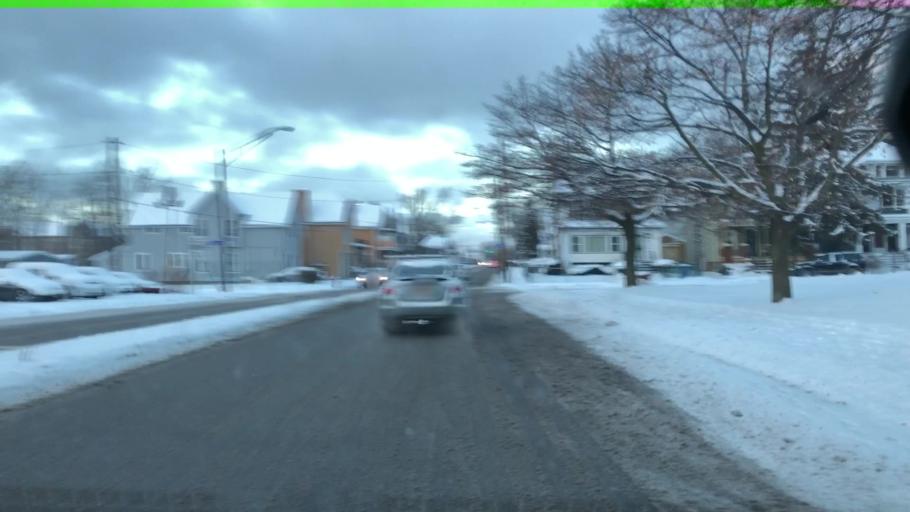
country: US
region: New York
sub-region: Erie County
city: Buffalo
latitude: 42.9038
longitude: -78.8465
